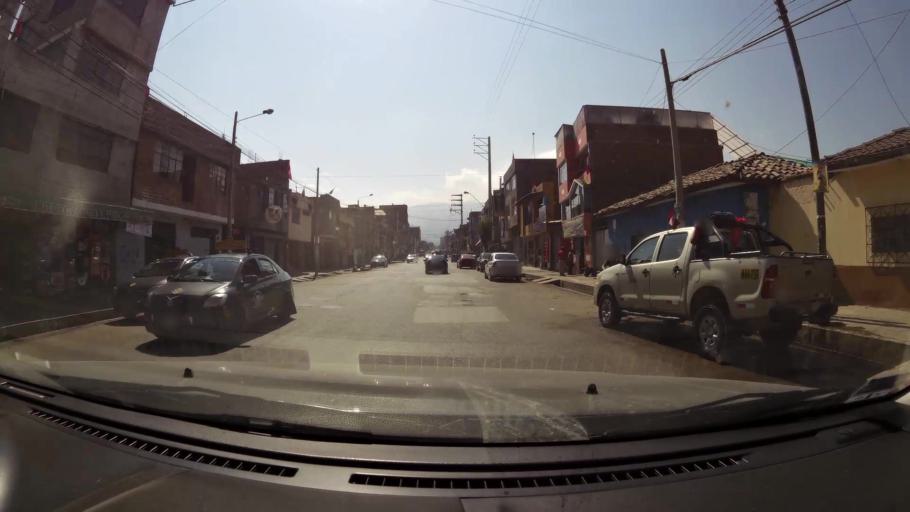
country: PE
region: Junin
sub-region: Provincia de Huancayo
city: El Tambo
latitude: -12.0760
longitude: -75.2256
